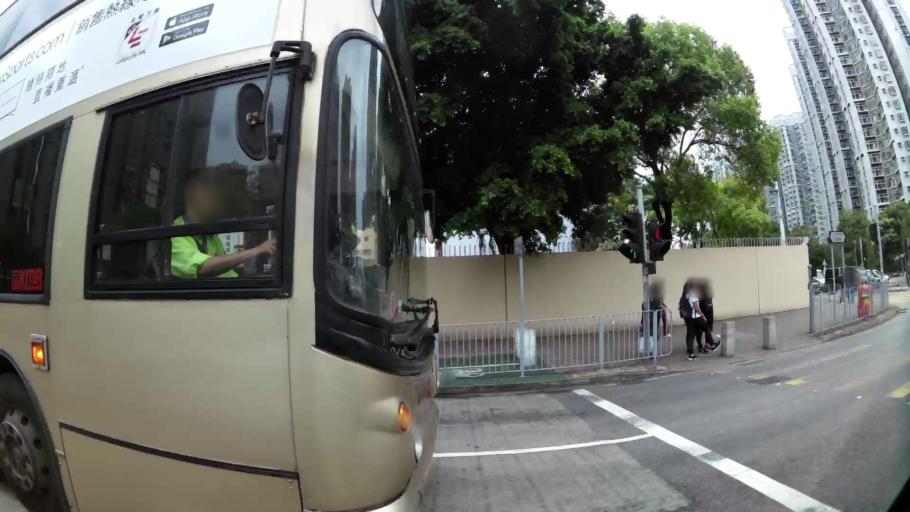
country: HK
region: Yuen Long
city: Yuen Long Kau Hui
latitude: 22.4506
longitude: 114.0023
